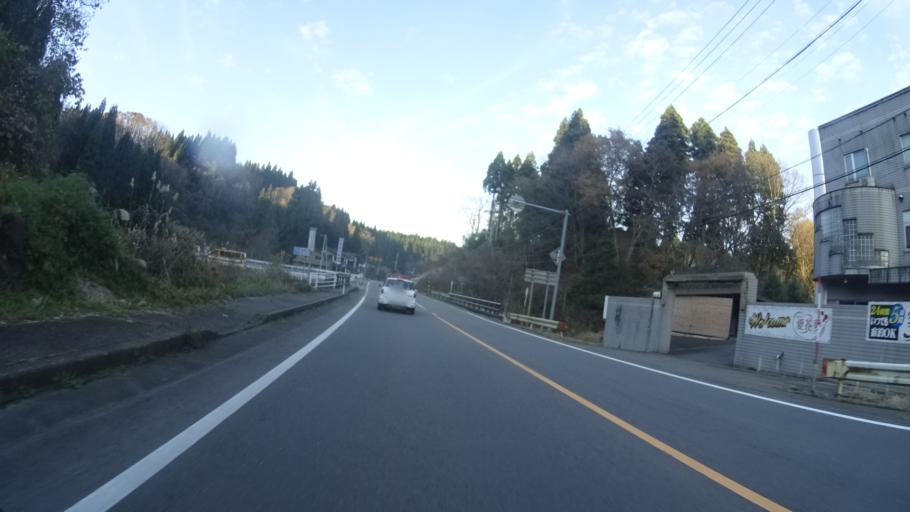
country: JP
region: Niigata
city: Ojiya
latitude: 37.4106
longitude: 138.7033
